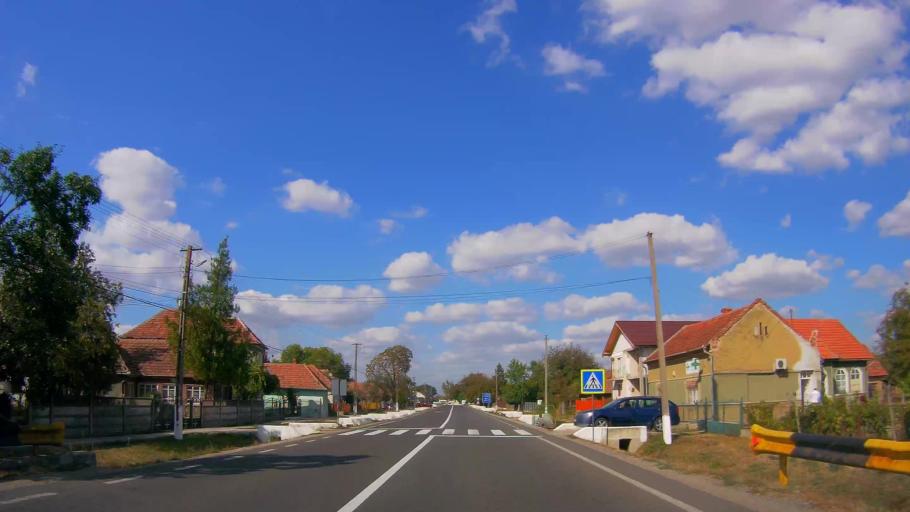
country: RO
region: Satu Mare
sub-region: Comuna Acas
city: Acas
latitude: 47.5349
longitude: 22.7834
